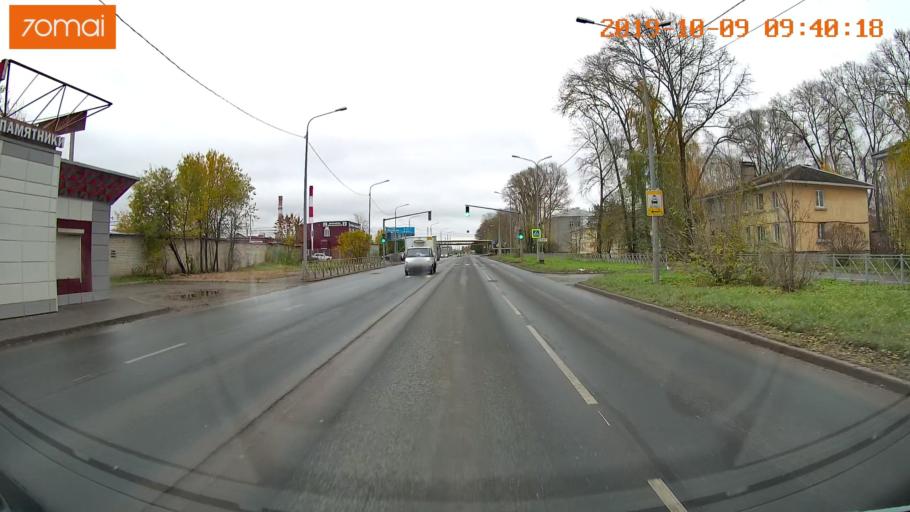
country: RU
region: Vologda
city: Vologda
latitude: 59.1957
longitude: 39.9238
